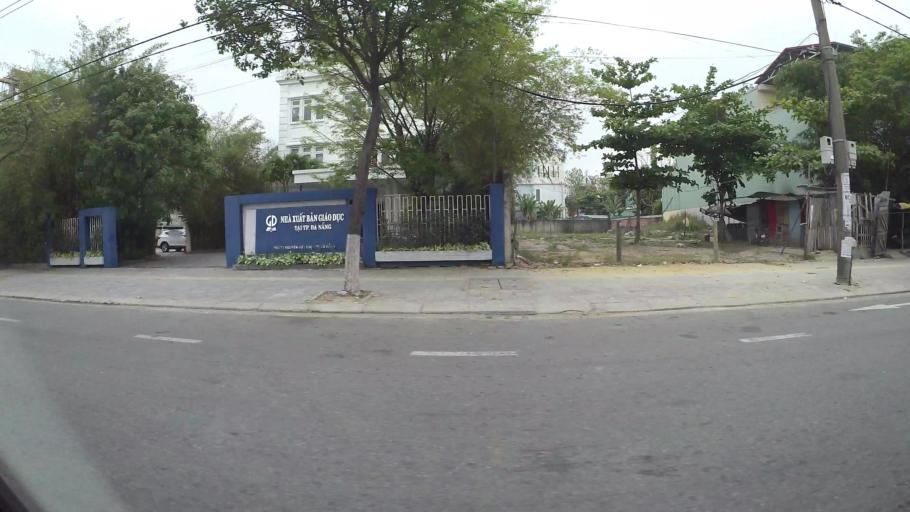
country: VN
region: Da Nang
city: Cam Le
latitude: 16.0261
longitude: 108.2090
